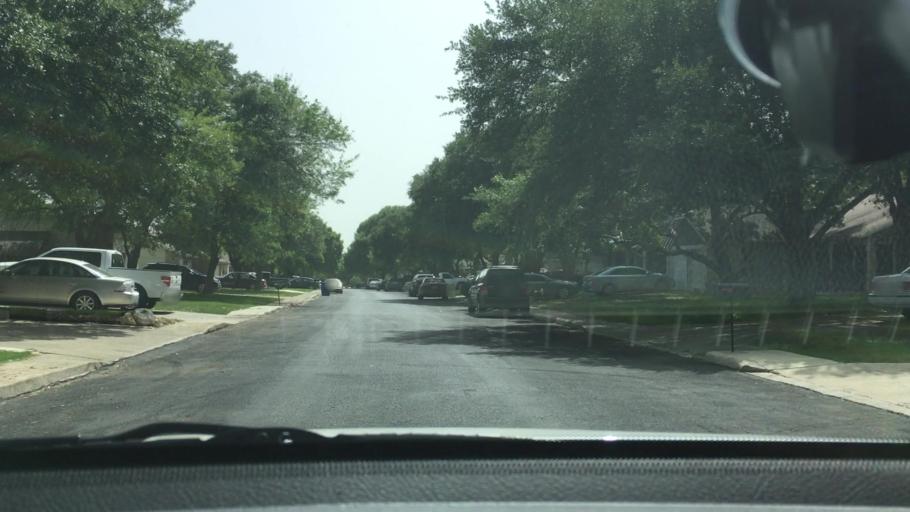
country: US
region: Texas
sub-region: Bexar County
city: Live Oak
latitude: 29.5939
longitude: -98.3779
